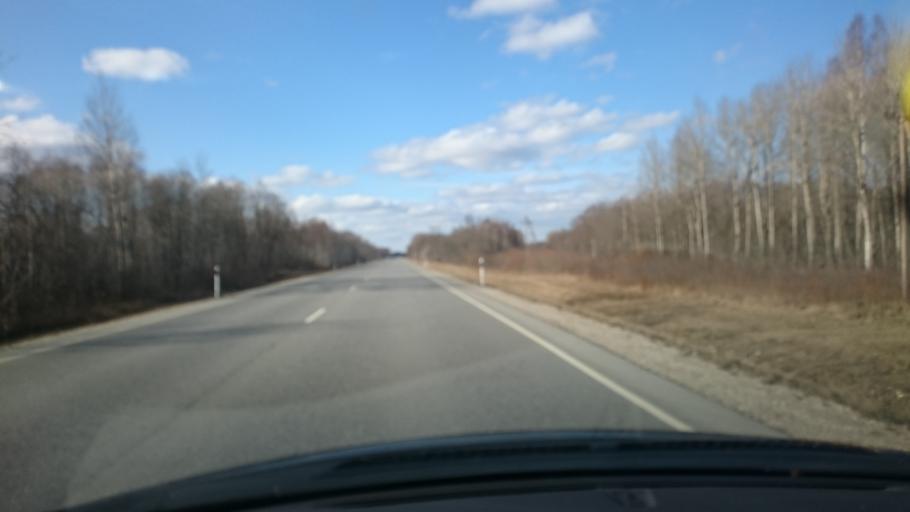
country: EE
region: Laeaene
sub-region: Lihula vald
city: Lihula
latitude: 58.7490
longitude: 23.9946
